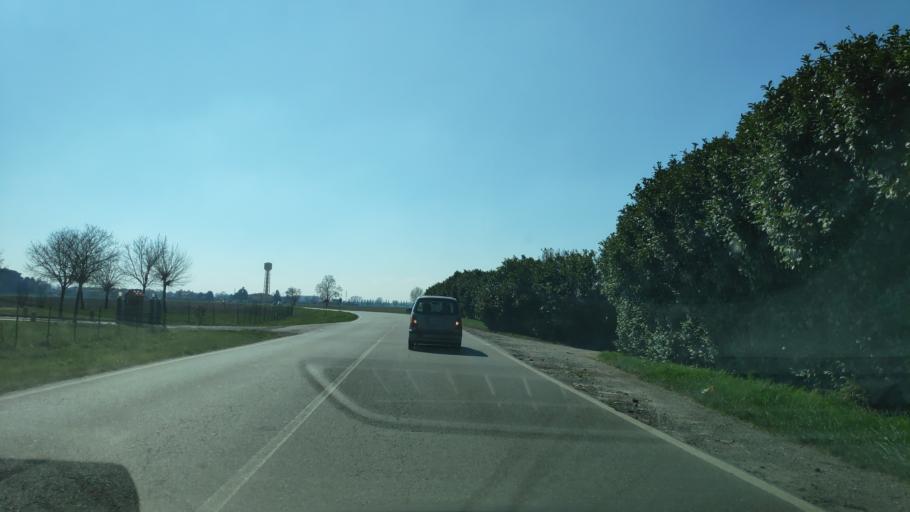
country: IT
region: Lombardy
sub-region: Citta metropolitana di Milano
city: Premenugo
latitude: 45.4778
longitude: 9.3810
